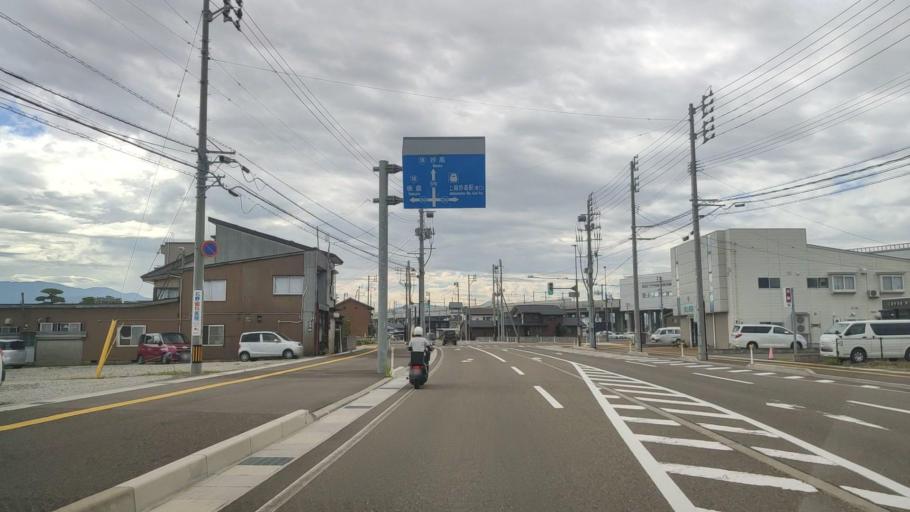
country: JP
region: Niigata
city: Joetsu
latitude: 37.0830
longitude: 138.2501
